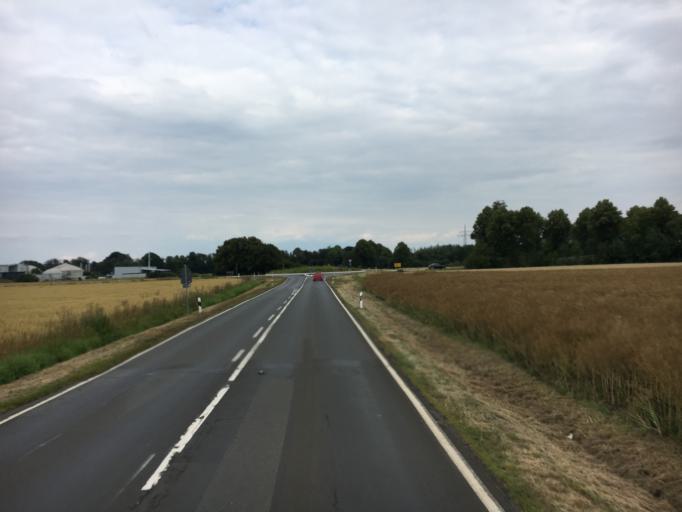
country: DE
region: Hesse
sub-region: Regierungsbezirk Giessen
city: Kirchhain
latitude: 50.8327
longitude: 8.9013
